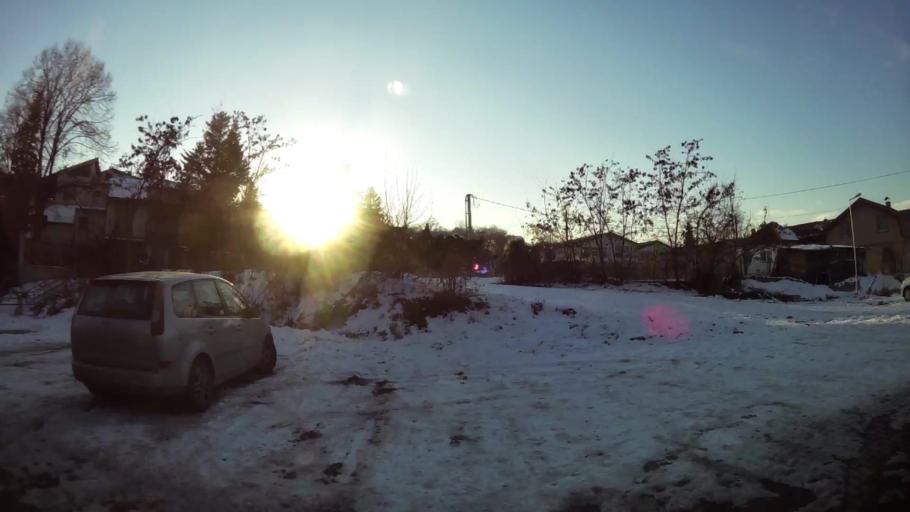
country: MK
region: Karpos
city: Skopje
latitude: 41.9959
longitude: 21.3953
